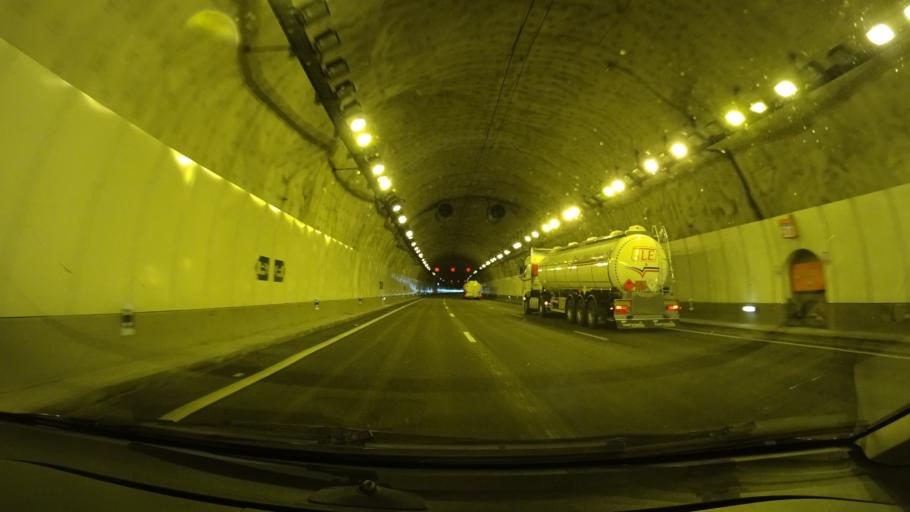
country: ES
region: Andalusia
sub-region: Provincia de Sevilla
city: El Ronquillo
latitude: 37.6497
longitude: -6.1595
